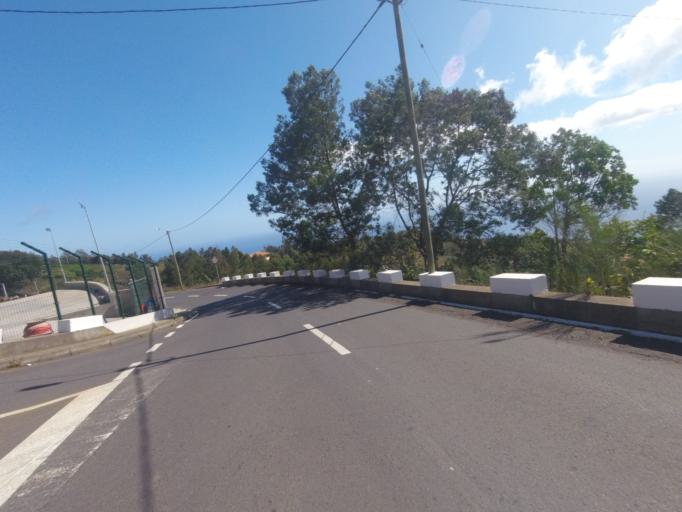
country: PT
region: Madeira
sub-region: Ribeira Brava
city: Campanario
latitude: 32.6814
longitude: -17.0407
